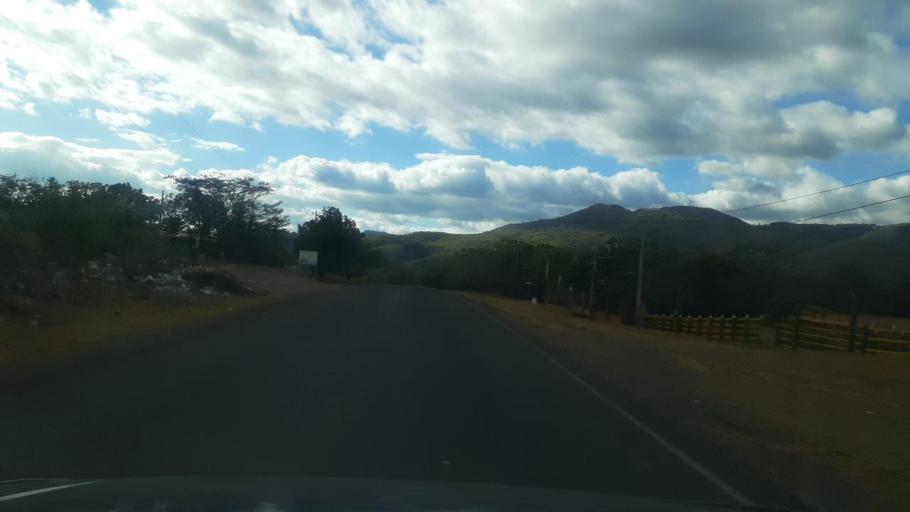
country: NI
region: Madriz
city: Somoto
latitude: 13.4714
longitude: -86.6103
